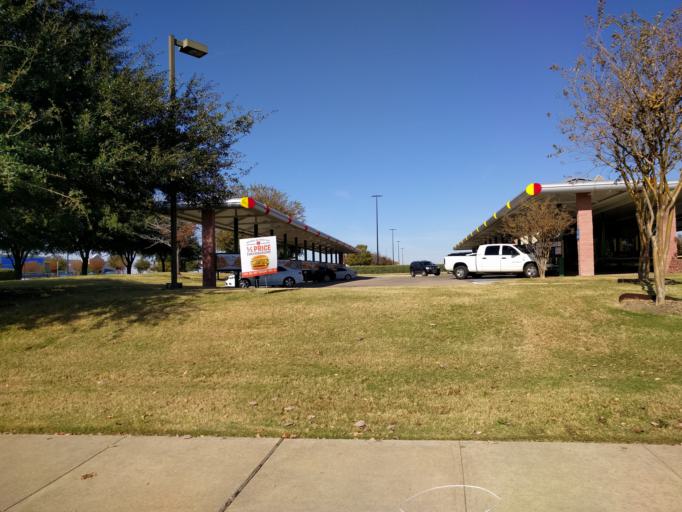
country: US
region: Texas
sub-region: Dallas County
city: Richardson
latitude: 33.0028
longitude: -96.7695
